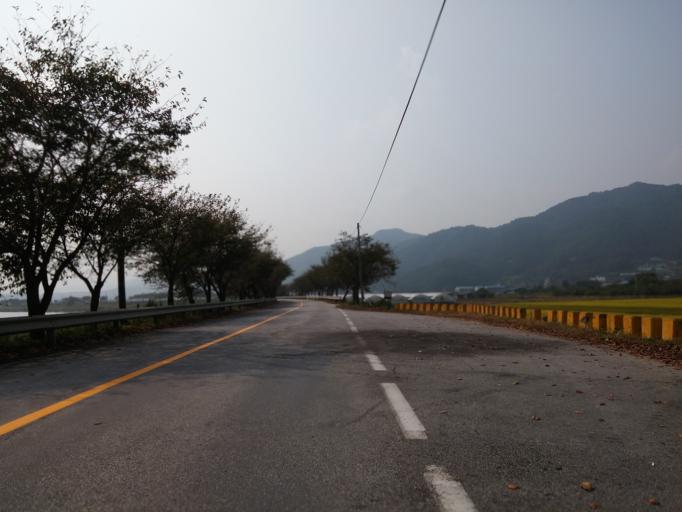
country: KR
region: Chungcheongbuk-do
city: Yong-dong
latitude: 36.3424
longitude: 127.7910
